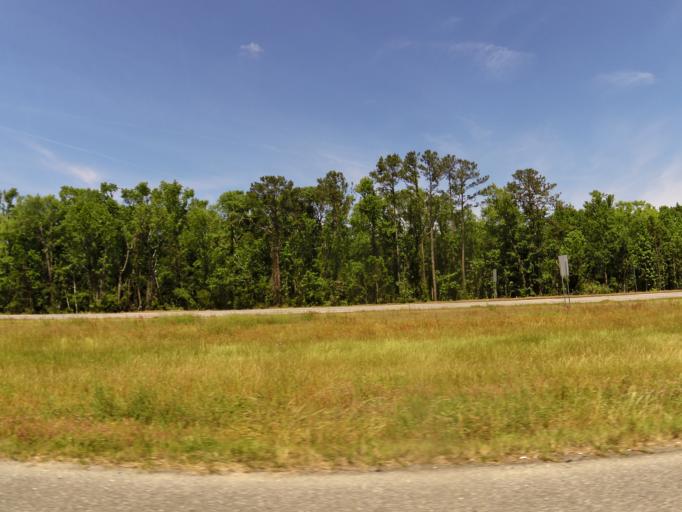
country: US
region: Georgia
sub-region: Camden County
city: Woodbine
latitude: 31.0625
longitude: -81.6330
